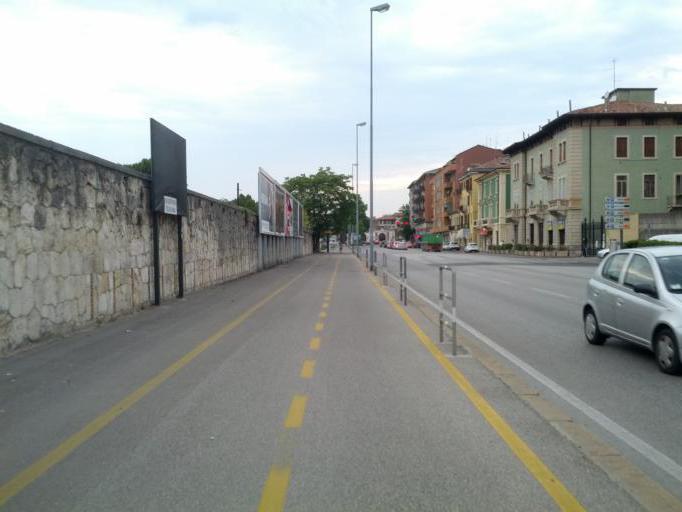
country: IT
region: Veneto
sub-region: Provincia di Verona
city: Poiano
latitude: 45.4388
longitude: 11.0190
